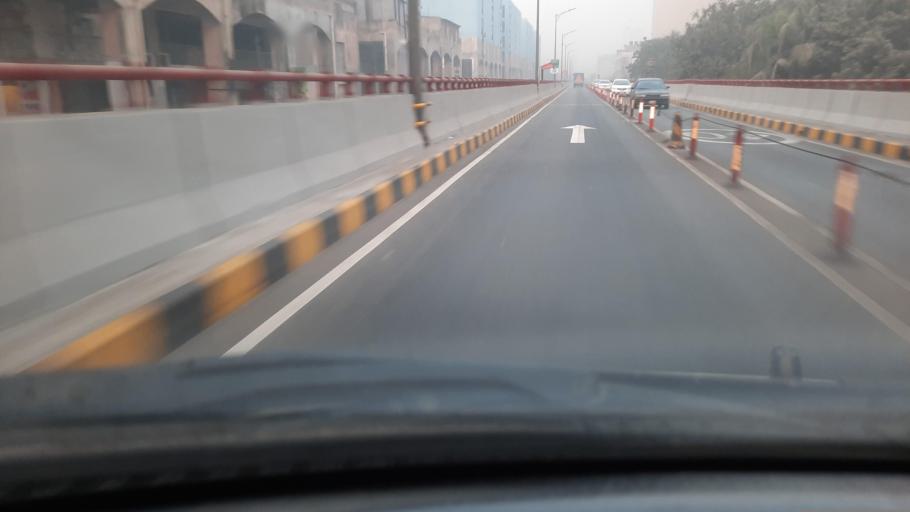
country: BD
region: Dhaka
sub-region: Dhaka
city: Dhaka
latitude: 23.7231
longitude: 90.4098
